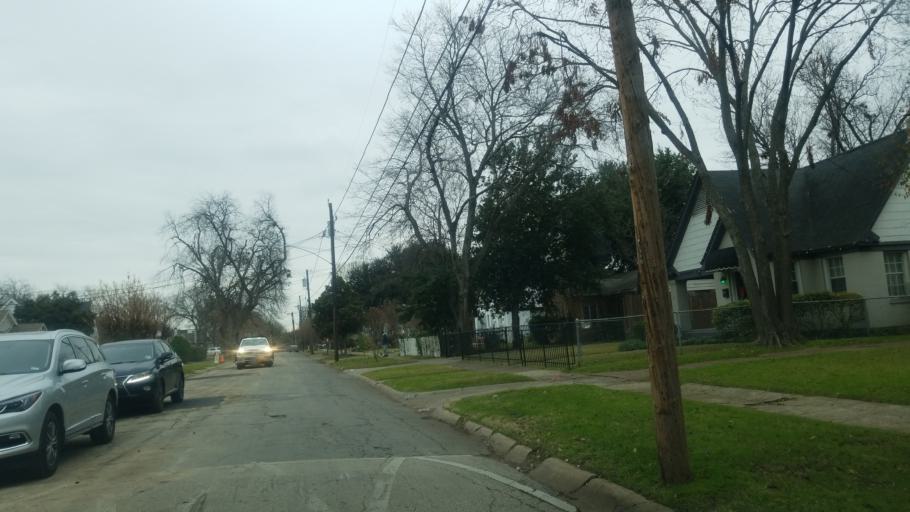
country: US
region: Texas
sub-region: Dallas County
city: Highland Park
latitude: 32.8200
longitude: -96.8298
